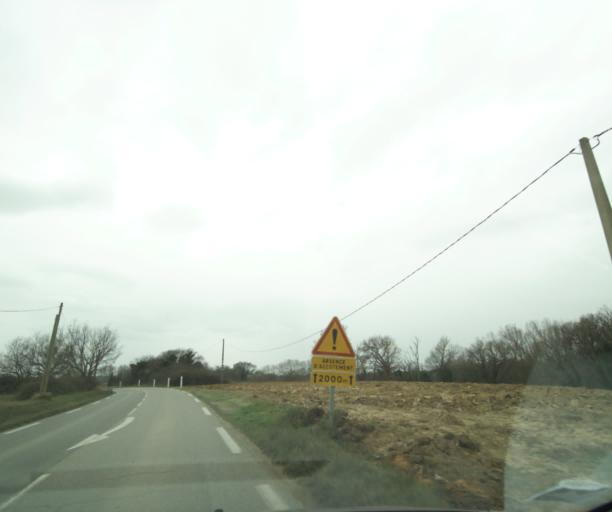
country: FR
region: Provence-Alpes-Cote d'Azur
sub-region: Departement des Bouches-du-Rhone
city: Eguilles
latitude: 43.5772
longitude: 5.4080
